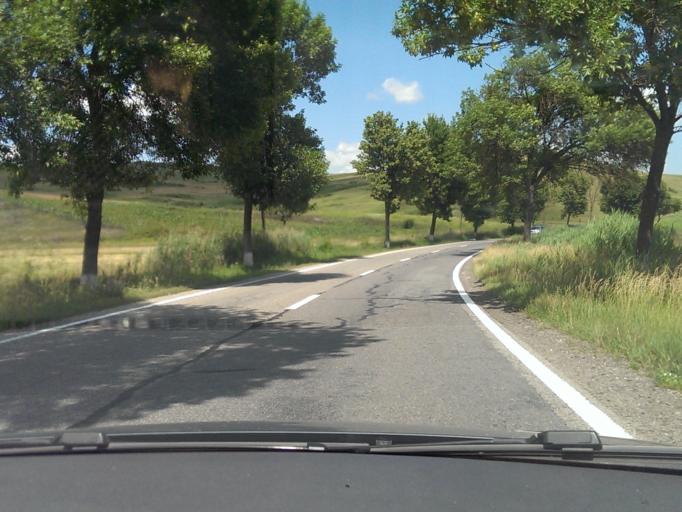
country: RO
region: Cluj
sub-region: Comuna Apahida
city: Apahida
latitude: 46.8099
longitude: 23.7820
